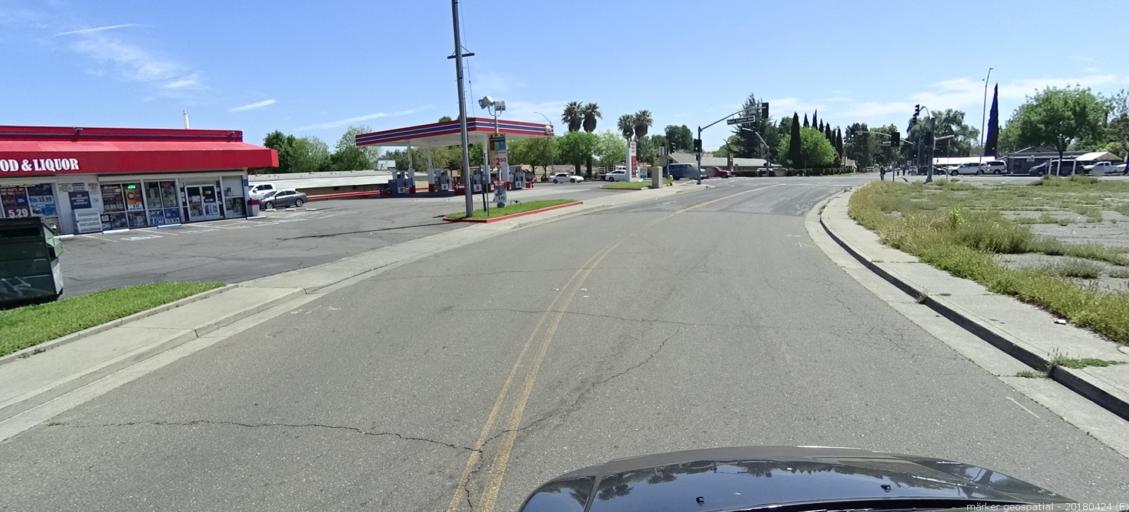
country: US
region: California
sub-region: Yolo County
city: West Sacramento
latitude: 38.5808
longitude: -121.5342
